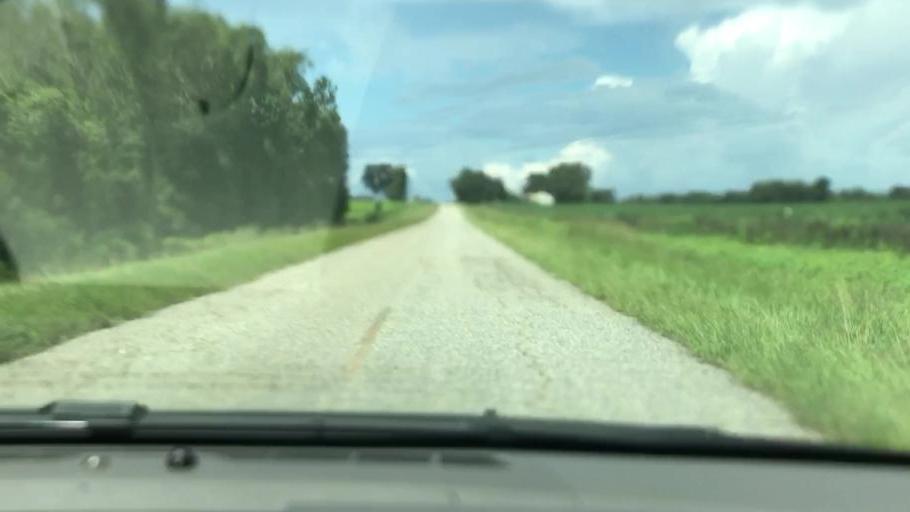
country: US
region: Georgia
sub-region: Seminole County
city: Donalsonville
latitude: 31.1876
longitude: -85.0042
